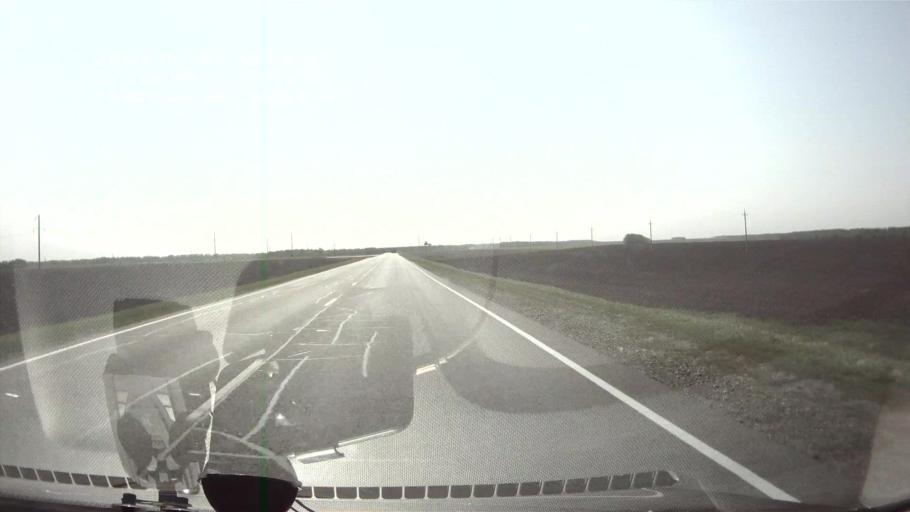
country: RU
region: Krasnodarskiy
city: Novopokrovskaya
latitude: 45.9212
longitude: 40.7146
